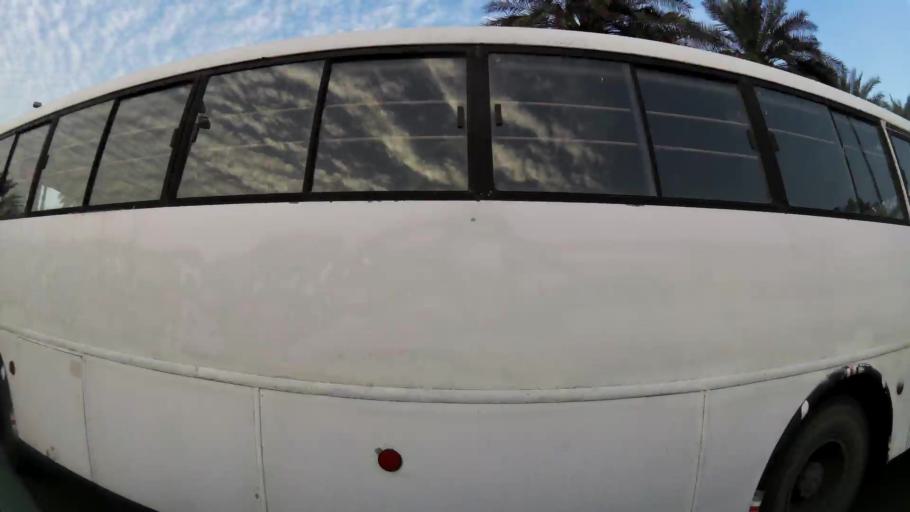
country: AE
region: Abu Dhabi
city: Abu Dhabi
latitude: 24.4418
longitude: 54.3752
